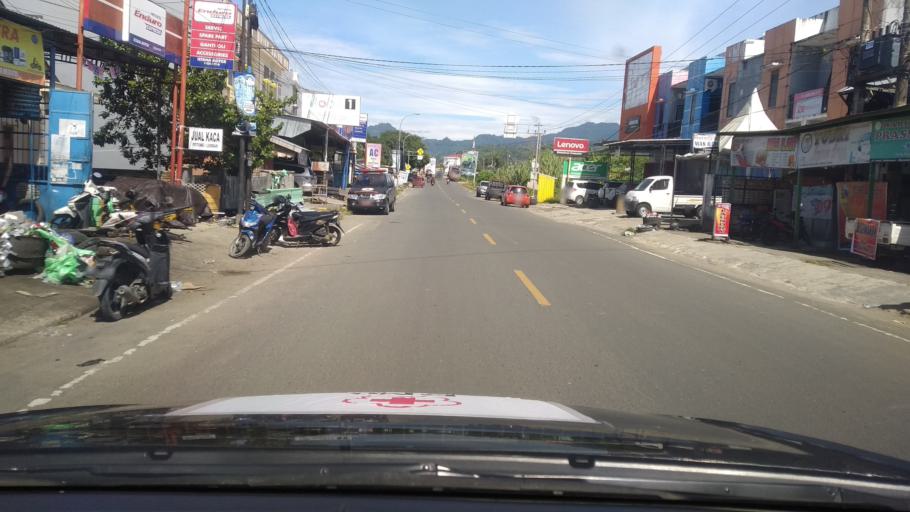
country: ID
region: Sulawesi Barat
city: Mamuju
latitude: -2.6825
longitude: 118.8724
